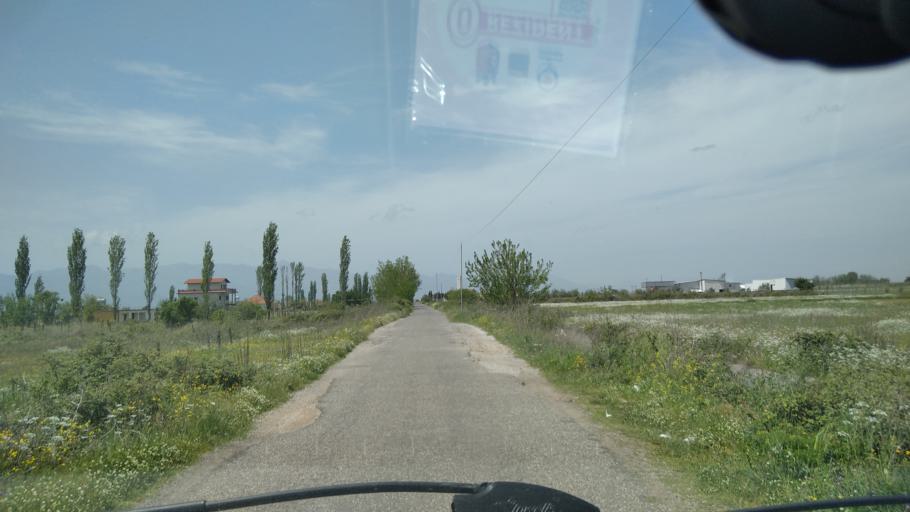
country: AL
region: Shkoder
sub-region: Rrethi i Malesia e Madhe
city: Gruemire
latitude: 42.1425
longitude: 19.5111
